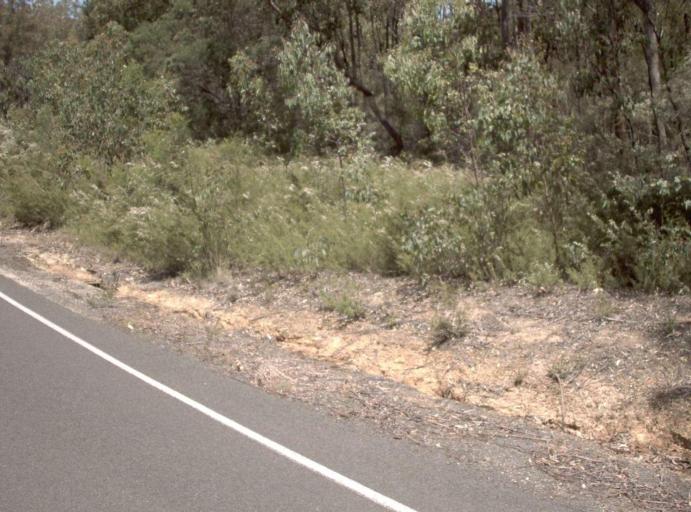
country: AU
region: Victoria
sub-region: East Gippsland
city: Lakes Entrance
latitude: -37.5936
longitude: 147.8930
